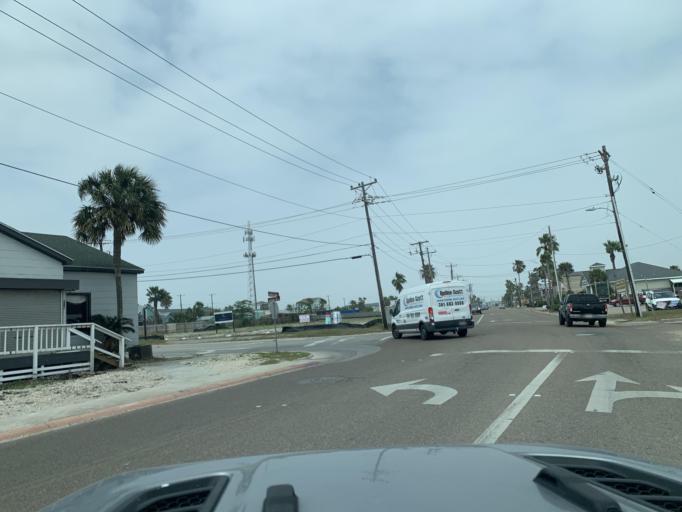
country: US
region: Texas
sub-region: Nueces County
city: Port Aransas
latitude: 27.8380
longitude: -97.0605
